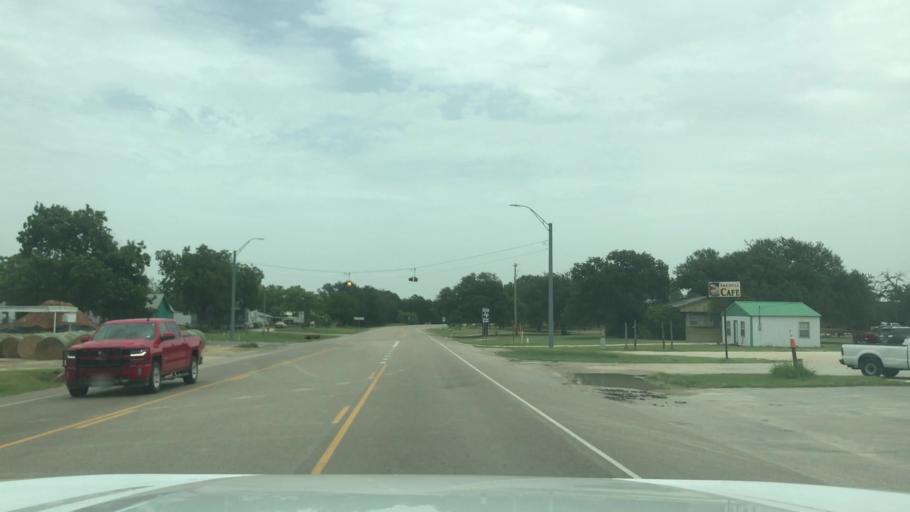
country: US
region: Texas
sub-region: Hamilton County
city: Hico
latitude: 31.9814
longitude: -97.8705
